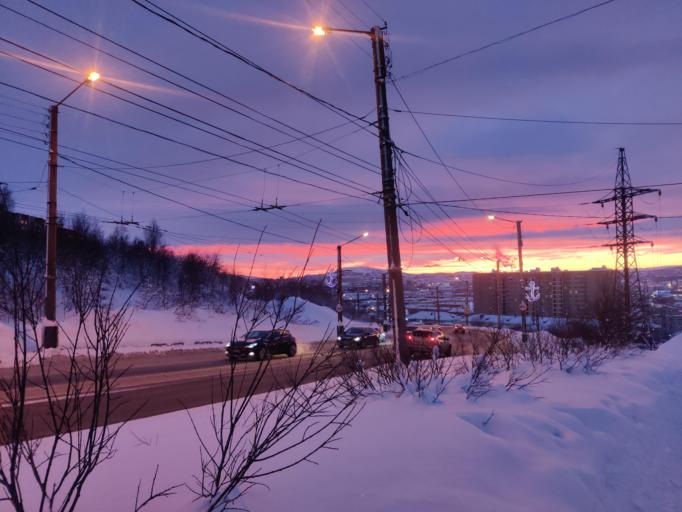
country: RU
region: Murmansk
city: Murmansk
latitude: 68.9875
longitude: 33.0919
